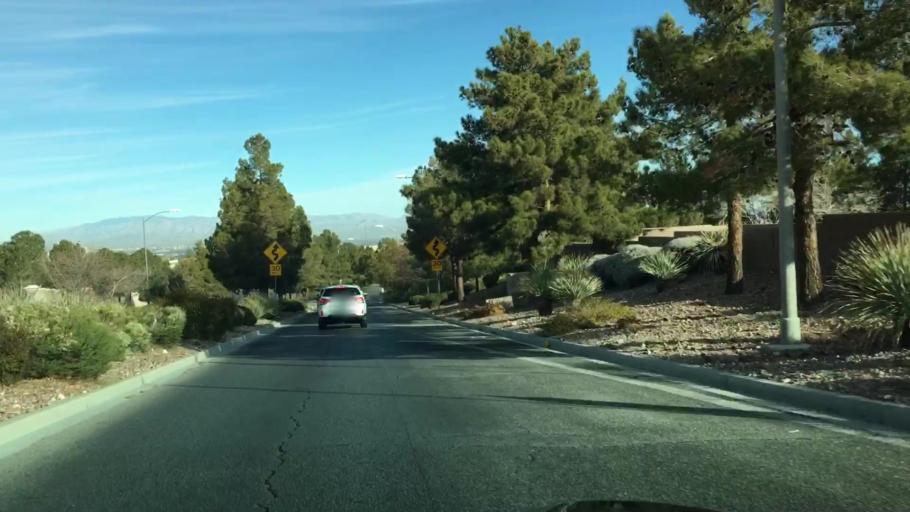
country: US
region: Nevada
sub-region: Clark County
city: Whitney
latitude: 35.9816
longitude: -115.1008
